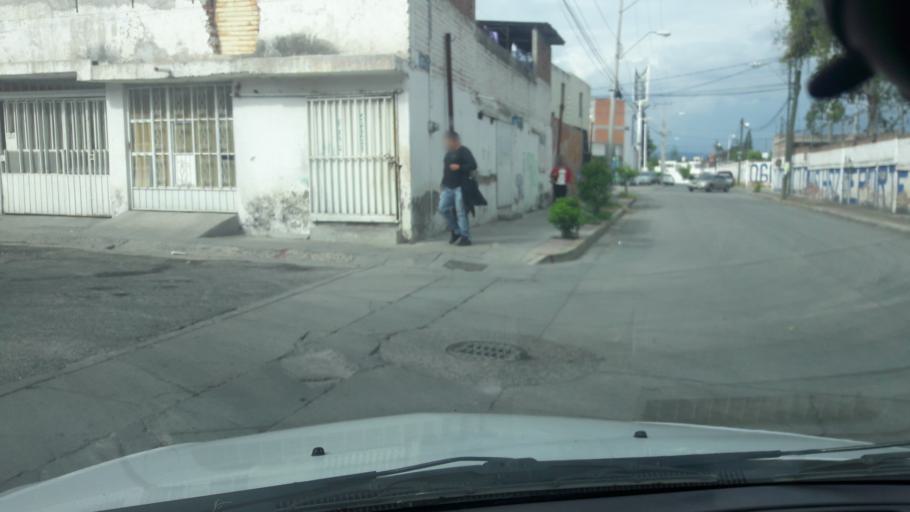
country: MX
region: Guanajuato
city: Leon
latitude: 21.1430
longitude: -101.6973
